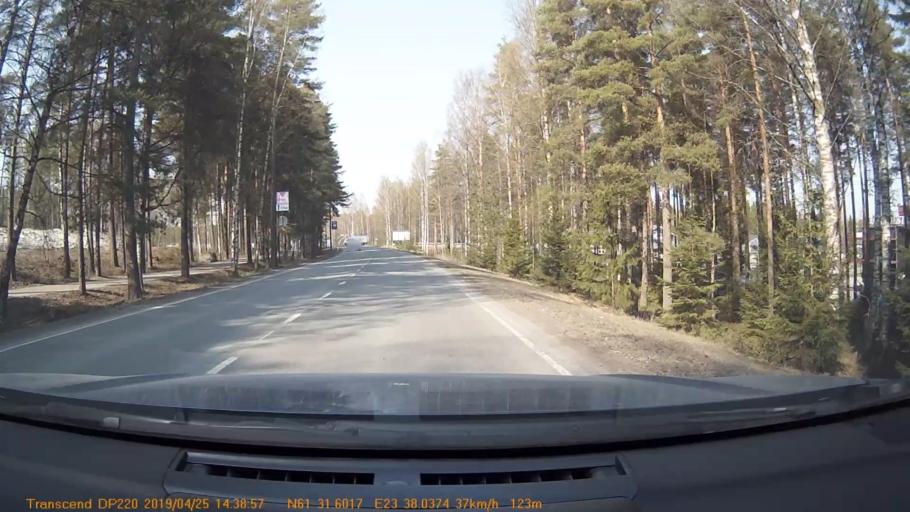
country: FI
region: Pirkanmaa
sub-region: Tampere
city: Yloejaervi
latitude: 61.5266
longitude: 23.6340
